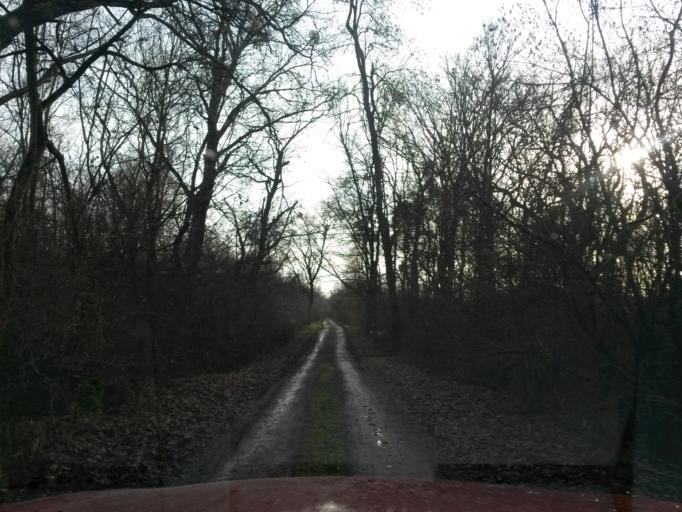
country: SK
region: Kosicky
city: Cierna nad Tisou
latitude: 48.5227
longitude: 22.0245
